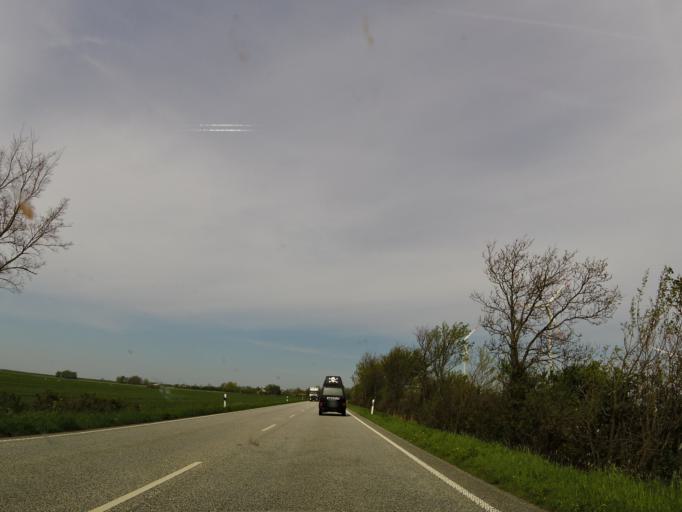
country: DE
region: Schleswig-Holstein
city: Groven
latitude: 54.2838
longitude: 8.9943
